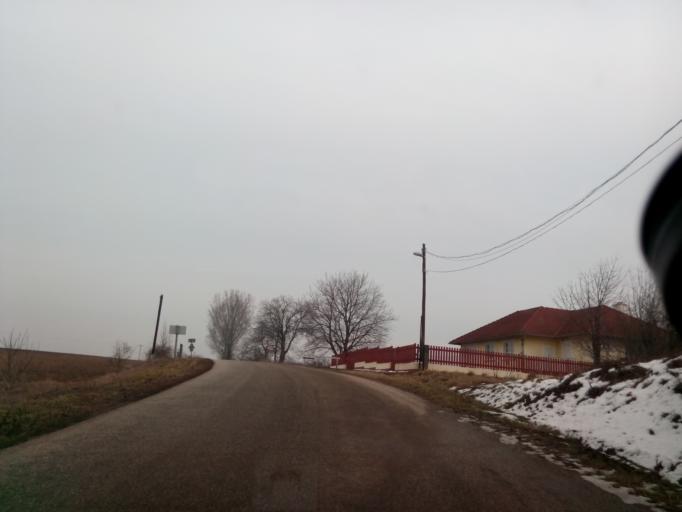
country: HU
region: Borsod-Abauj-Zemplen
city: Gonc
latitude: 48.4769
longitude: 21.2824
